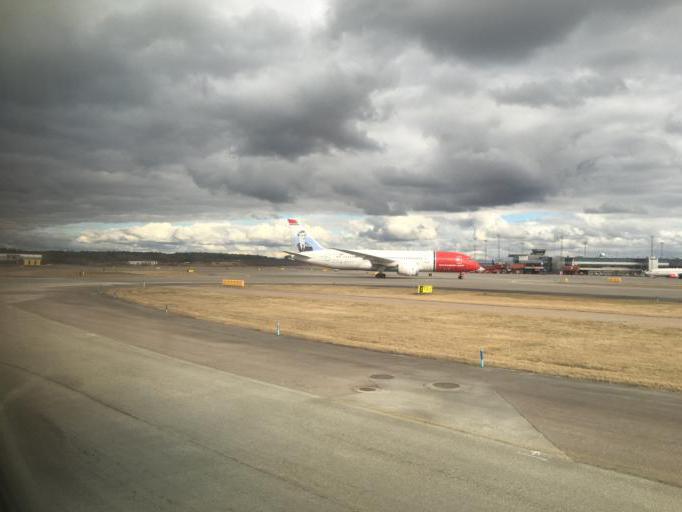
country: SE
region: Stockholm
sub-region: Sigtuna Kommun
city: Marsta
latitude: 59.6521
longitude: 17.9221
